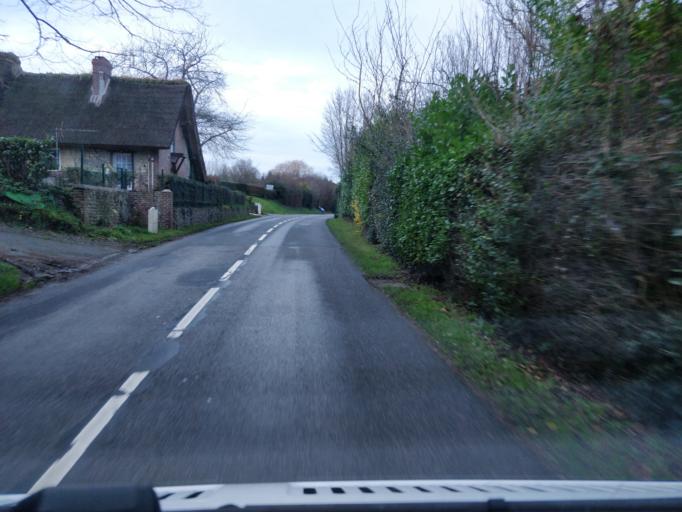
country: FR
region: Lower Normandy
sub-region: Departement du Calvados
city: Equemauville
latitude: 49.4017
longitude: 0.1514
